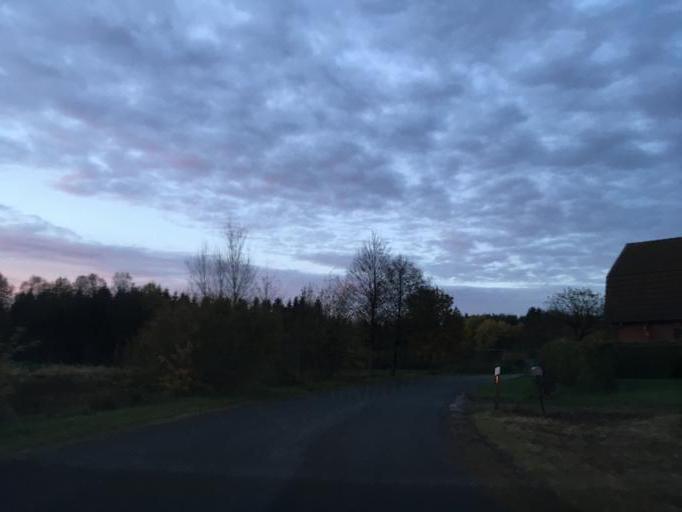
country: DE
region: Lower Saxony
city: Soderstorf
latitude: 53.1193
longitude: 10.1152
